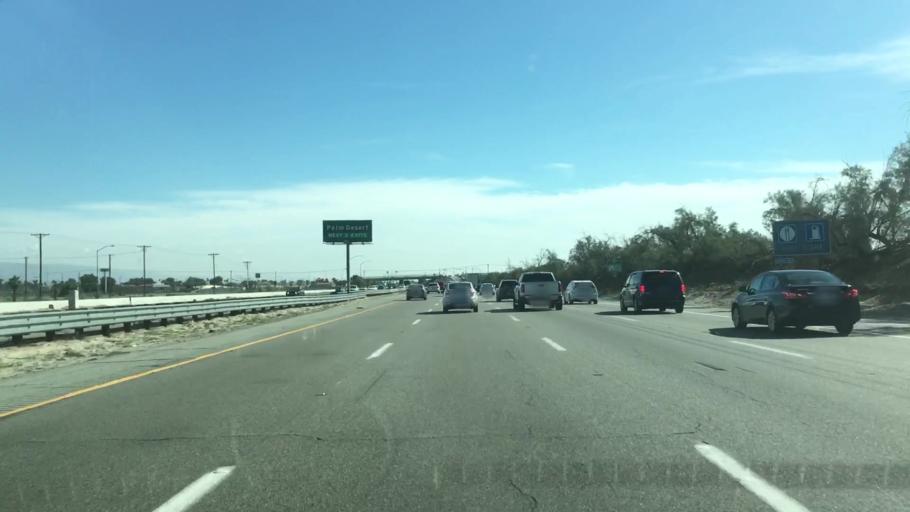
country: US
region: California
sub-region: Riverside County
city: Thousand Palms
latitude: 33.8112
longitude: -116.3972
